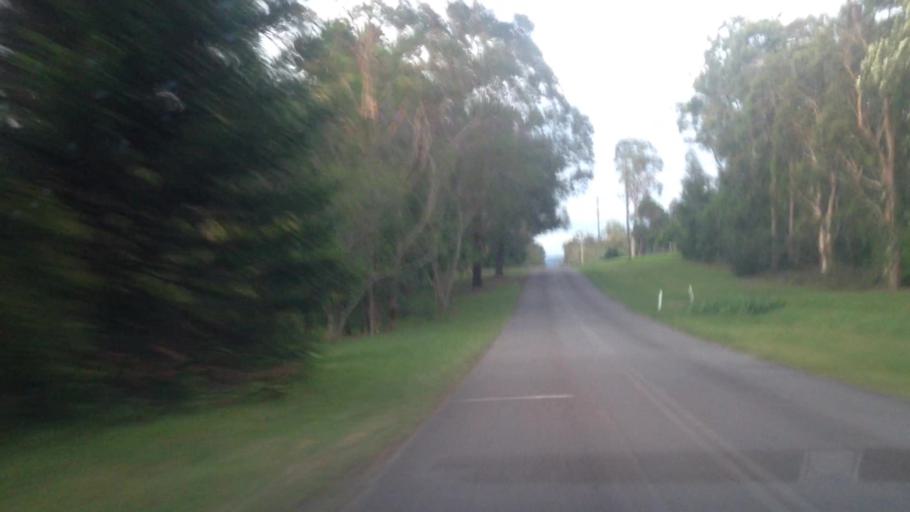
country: AU
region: New South Wales
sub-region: Lake Macquarie Shire
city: Cooranbong
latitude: -33.0805
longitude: 151.4725
